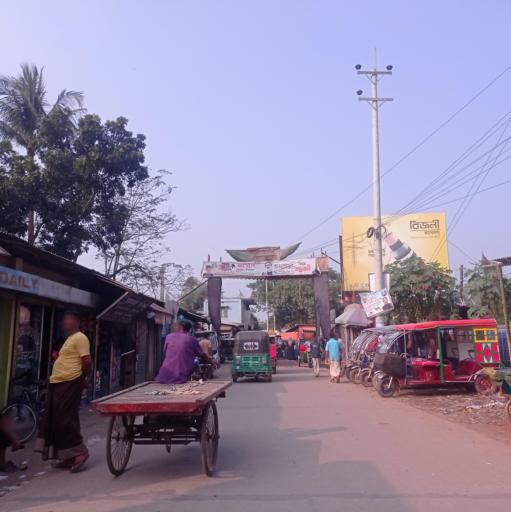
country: BD
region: Dhaka
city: Bhairab Bazar
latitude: 24.1033
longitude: 90.8523
